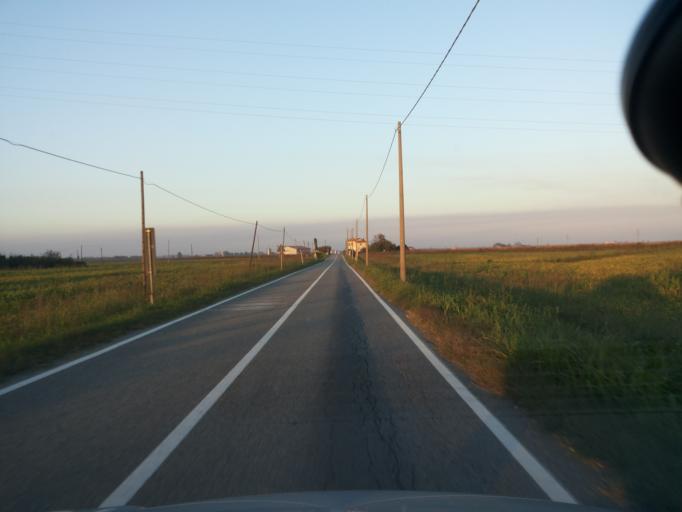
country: IT
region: Piedmont
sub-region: Provincia di Vercelli
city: Santhia
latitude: 45.3719
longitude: 8.1872
